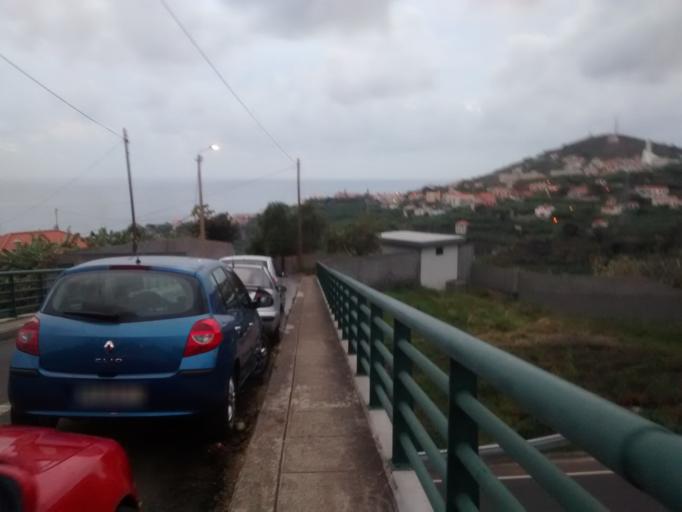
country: PT
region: Madeira
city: Camara de Lobos
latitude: 32.6538
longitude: -16.9622
